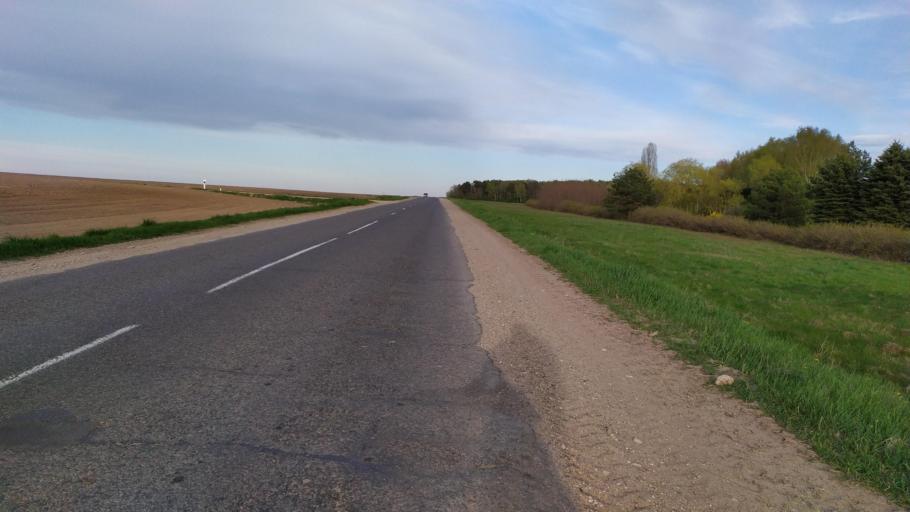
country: BY
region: Brest
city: Kamyanyets
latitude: 52.4175
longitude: 23.6882
